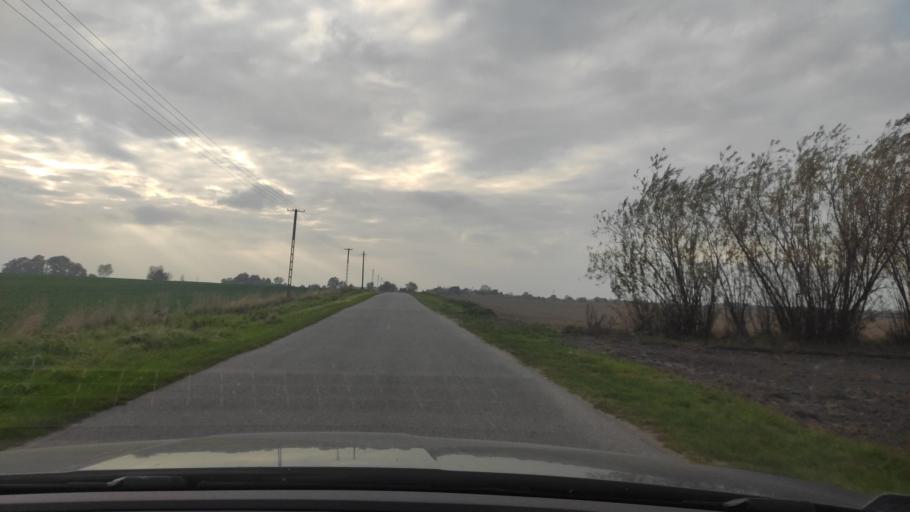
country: PL
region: Greater Poland Voivodeship
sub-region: Powiat poznanski
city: Kostrzyn
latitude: 52.4438
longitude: 17.1876
